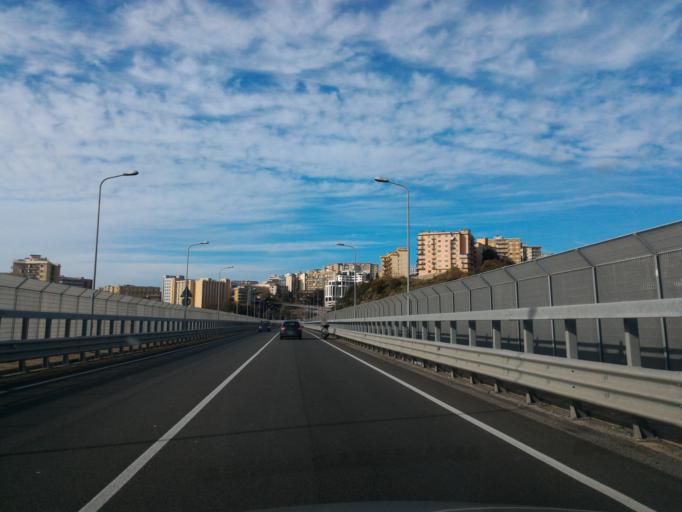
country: IT
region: Calabria
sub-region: Provincia di Catanzaro
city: Siano
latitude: 38.9112
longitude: 16.5966
